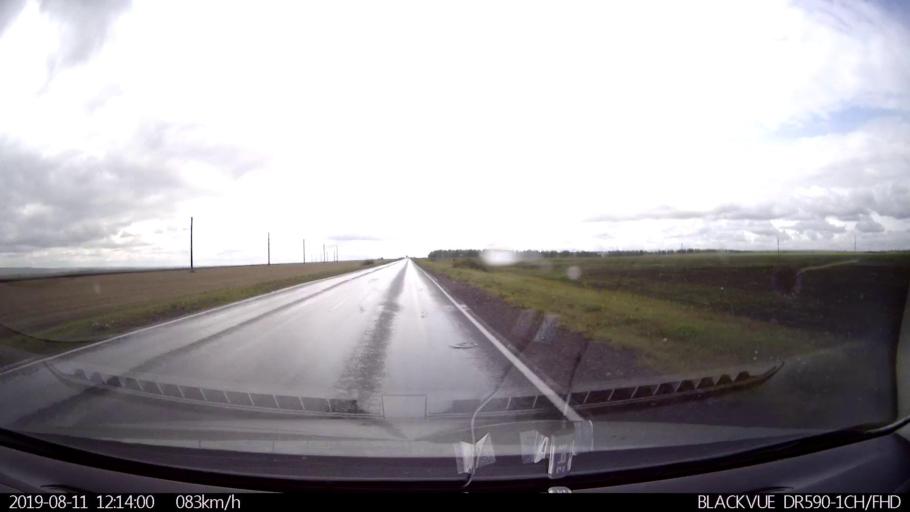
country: RU
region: Ulyanovsk
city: Ignatovka
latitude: 53.9564
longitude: 47.9858
